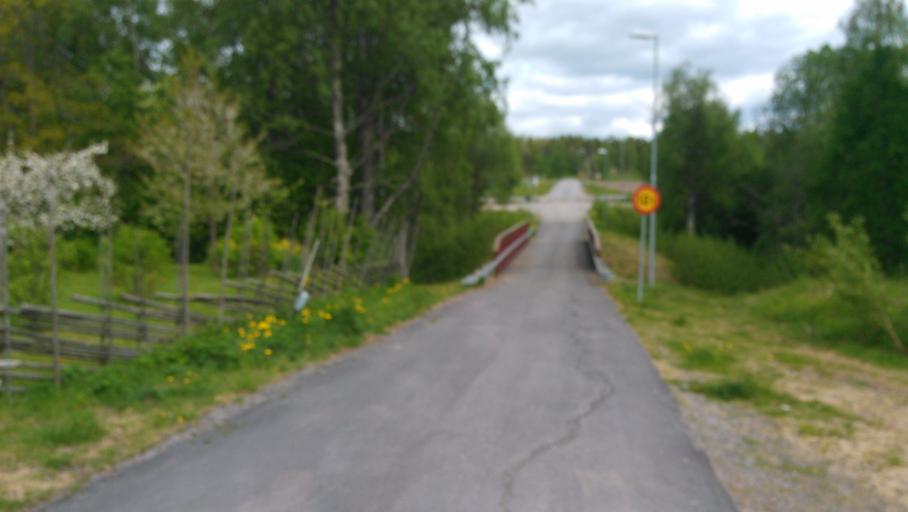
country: SE
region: Vaesterbotten
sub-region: Umea Kommun
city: Roback
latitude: 63.8774
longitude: 20.0525
